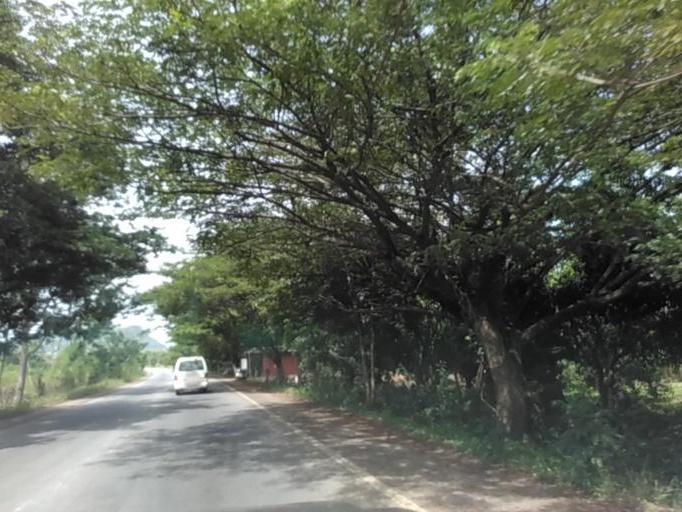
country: GH
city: Akropong
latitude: 6.1254
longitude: 0.0479
